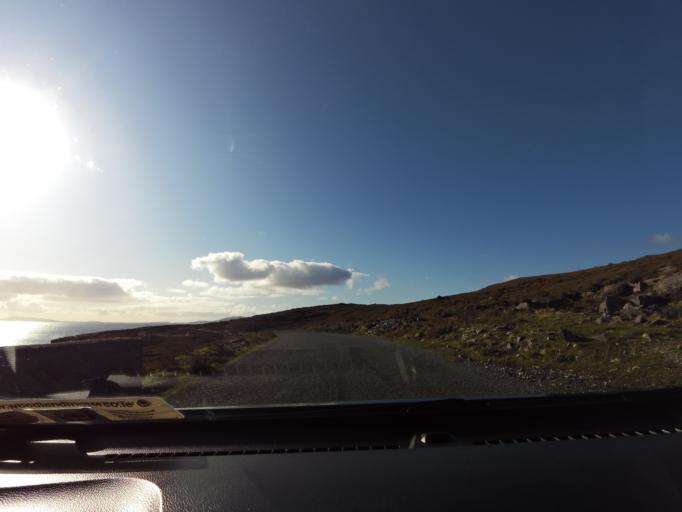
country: IE
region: Connaught
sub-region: Maigh Eo
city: Westport
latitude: 53.8744
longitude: -9.8426
